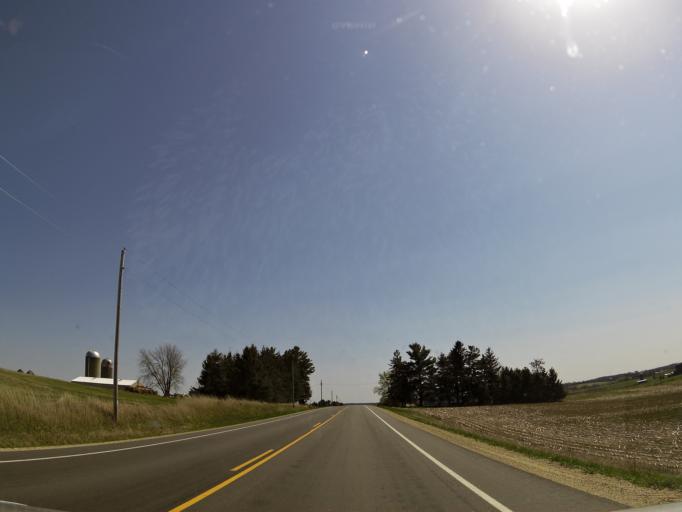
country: US
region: Wisconsin
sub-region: Saint Croix County
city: Hammond
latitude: 44.9015
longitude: -92.4355
